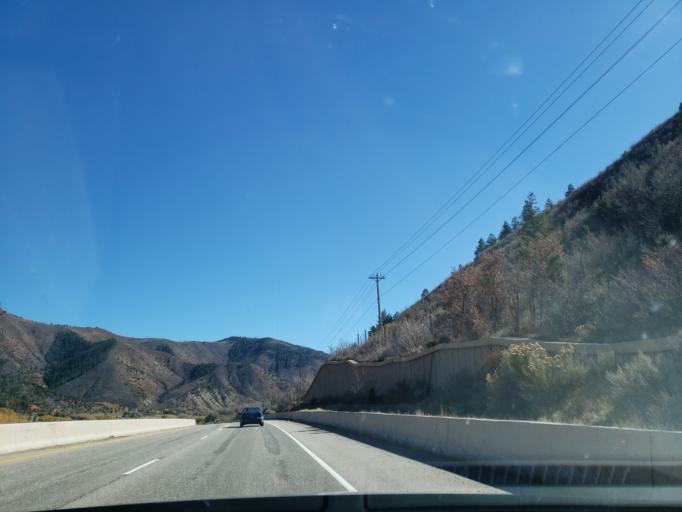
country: US
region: Colorado
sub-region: Eagle County
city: Basalt
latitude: 39.3271
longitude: -106.9585
